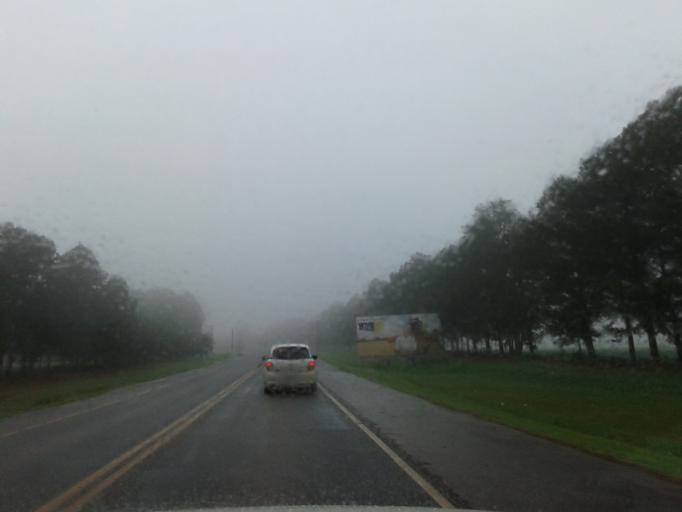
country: PY
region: Itapua
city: Arquitecto Tomas Romero Pereira
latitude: -26.5497
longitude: -55.2608
